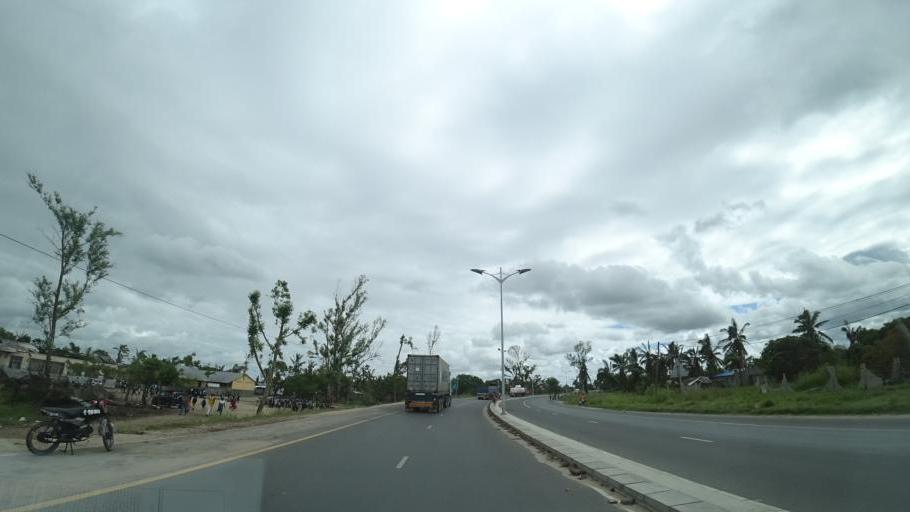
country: MZ
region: Sofala
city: Dondo
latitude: -19.6921
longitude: 34.7782
